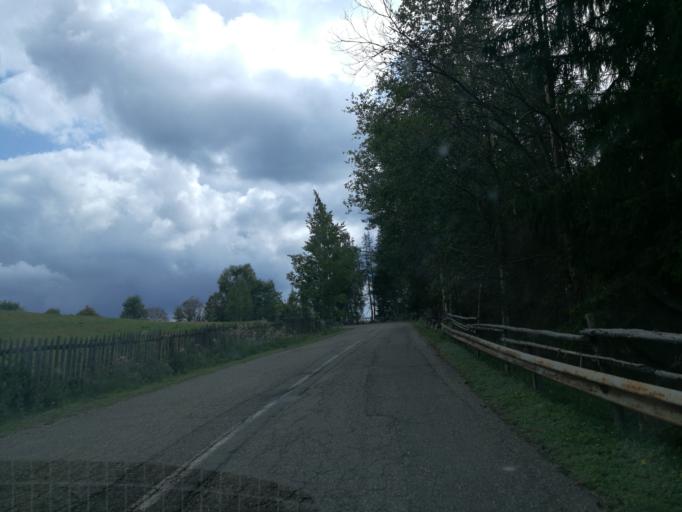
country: RO
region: Suceava
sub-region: Comuna Moldovita
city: Moldovita
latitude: 47.7287
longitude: 25.6119
